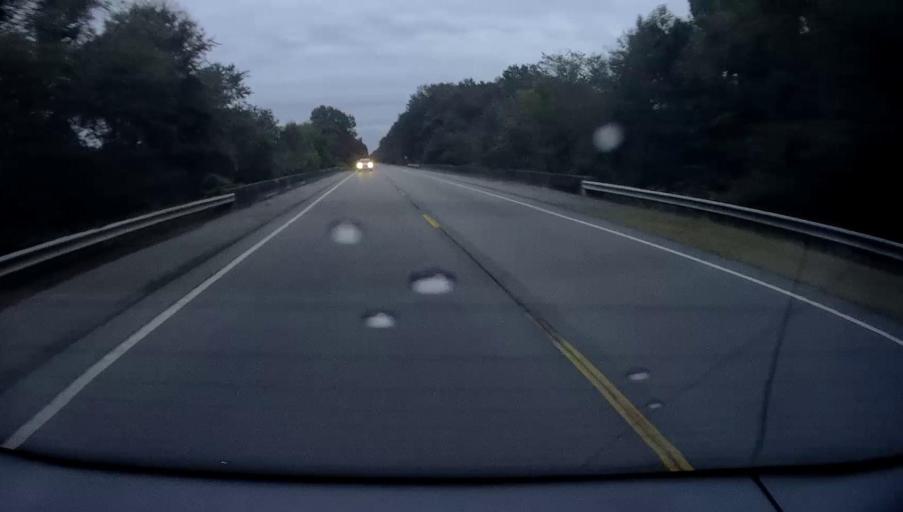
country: US
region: Georgia
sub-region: Houston County
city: Robins Air Force Base
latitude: 32.5419
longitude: -83.5304
